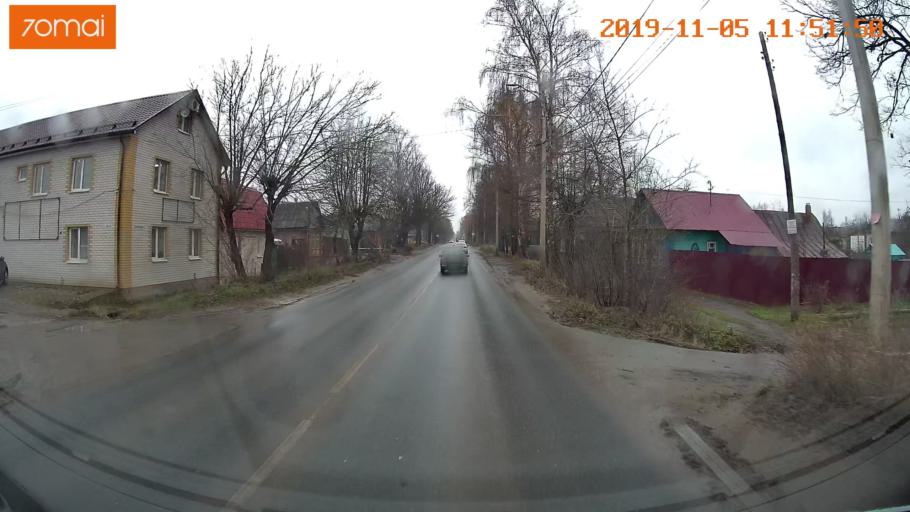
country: RU
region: Ivanovo
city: Bogorodskoye
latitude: 57.0035
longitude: 41.0288
